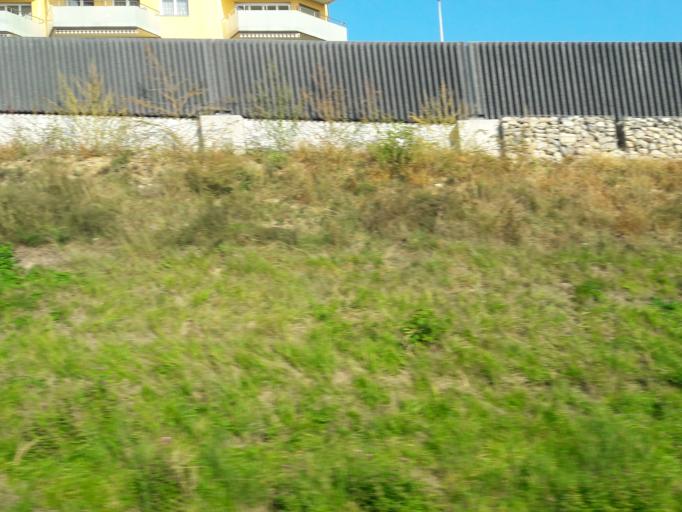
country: CH
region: Vaud
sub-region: Morges District
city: Saint-Prex
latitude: 46.4974
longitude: 6.4770
